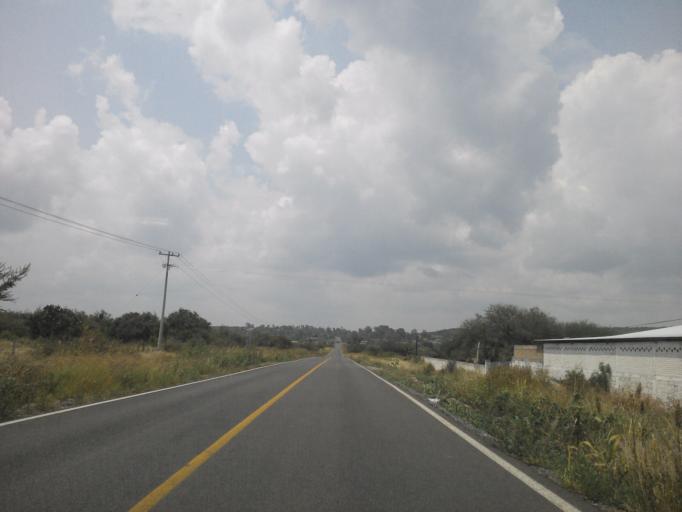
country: MX
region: Guanajuato
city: Ciudad Manuel Doblado
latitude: 20.8170
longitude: -101.9991
